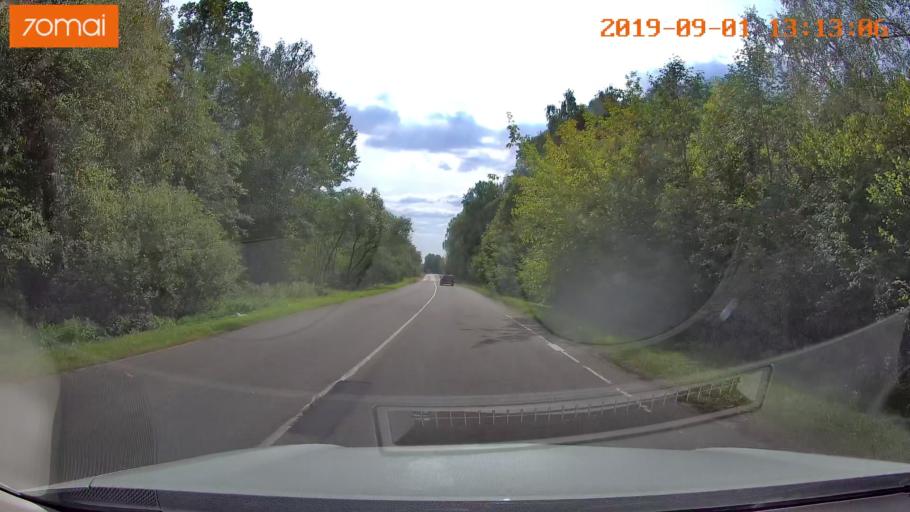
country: RU
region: Kaluga
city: Maloyaroslavets
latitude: 54.9773
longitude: 36.4672
